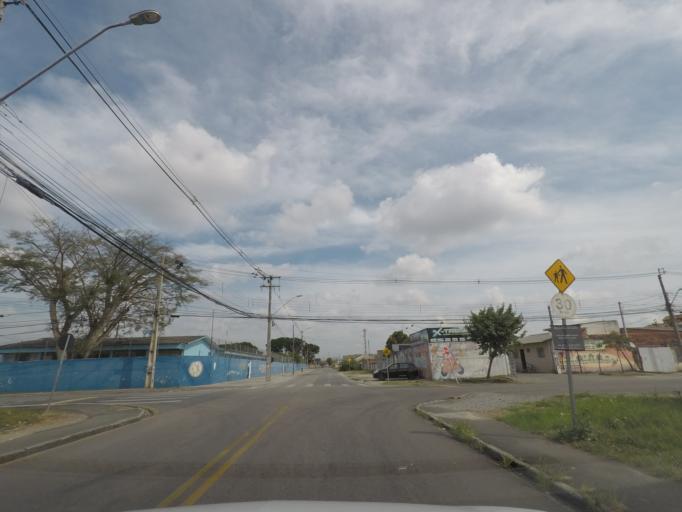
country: BR
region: Parana
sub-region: Pinhais
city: Pinhais
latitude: -25.4755
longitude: -49.1949
